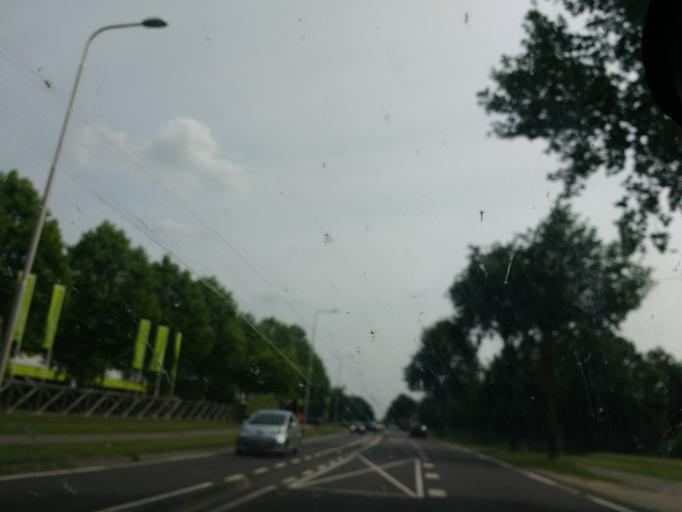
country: NL
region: Gelderland
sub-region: Gemeente Nijmegen
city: Nijmegen
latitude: 51.7959
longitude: 5.8488
